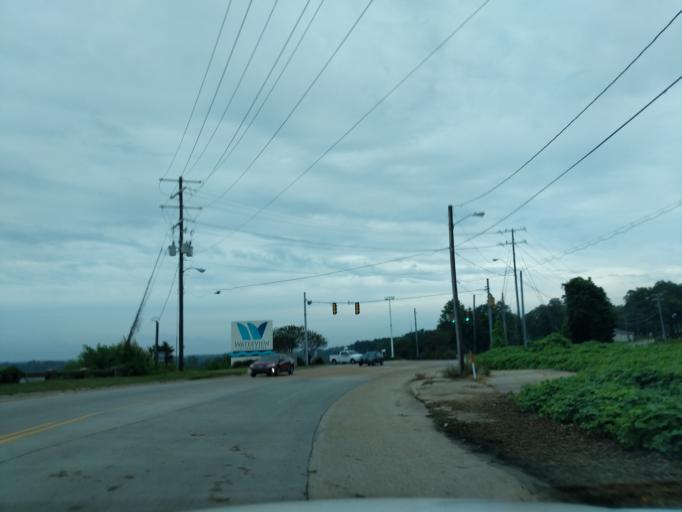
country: US
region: Mississippi
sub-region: Warren County
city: Vicksburg
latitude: 32.3223
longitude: -90.8961
